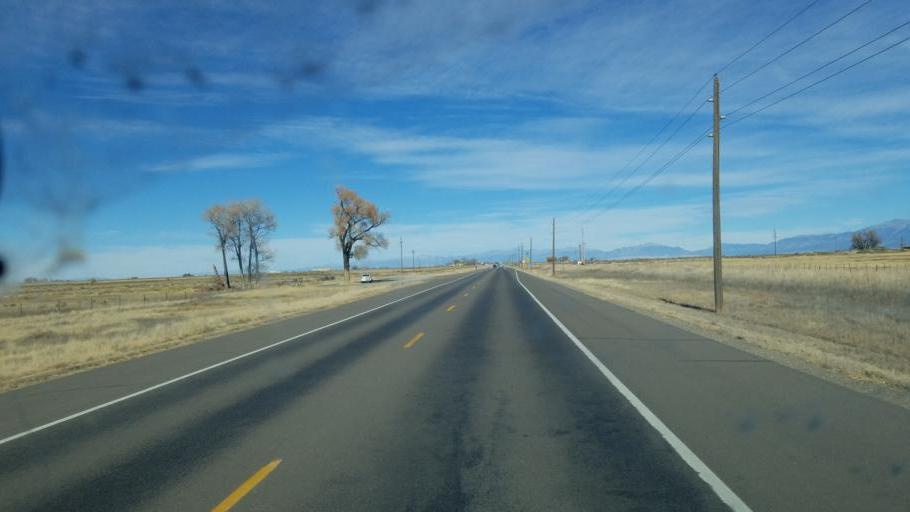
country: US
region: Colorado
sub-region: Alamosa County
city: Alamosa
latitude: 37.3316
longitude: -105.9427
